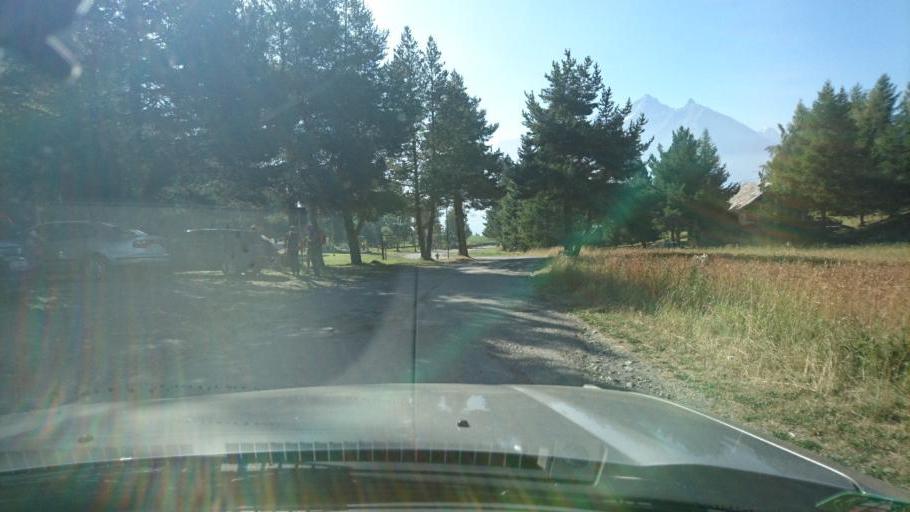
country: IT
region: Aosta Valley
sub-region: Valle d'Aosta
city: Saint-Nicolas
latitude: 45.7344
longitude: 7.1856
